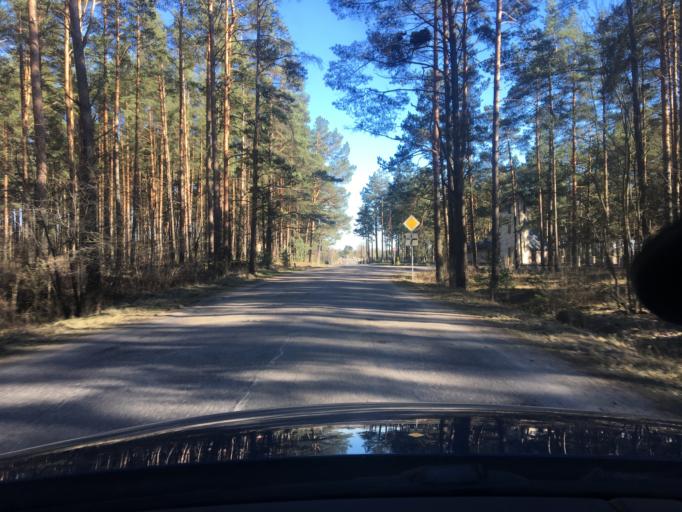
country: LV
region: Salaspils
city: Salaspils
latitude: 56.8648
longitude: 24.3082
